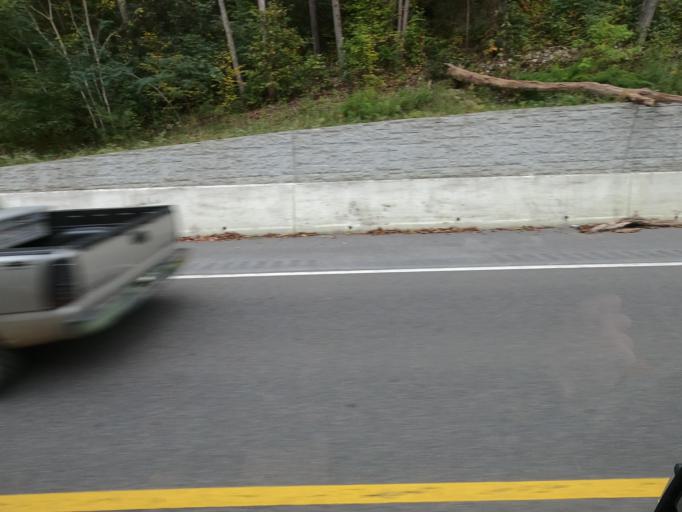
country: US
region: Tennessee
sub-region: Carter County
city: Central
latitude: 36.2665
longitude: -82.2302
